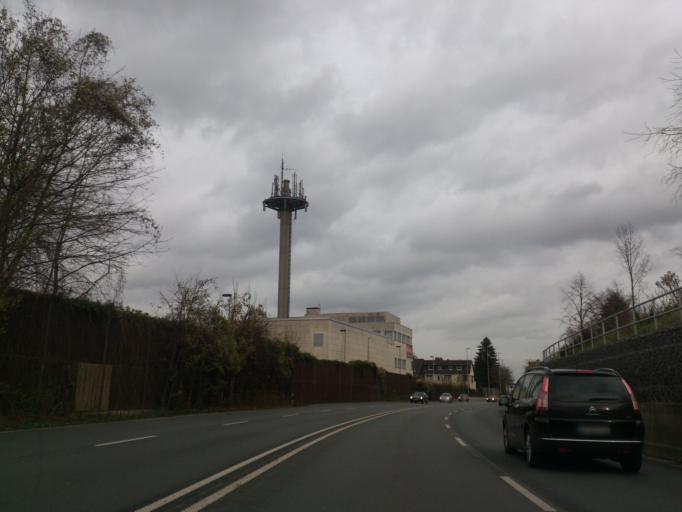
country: DE
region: North Rhine-Westphalia
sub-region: Regierungsbezirk Detmold
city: Hoexter
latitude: 51.7772
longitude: 9.3751
